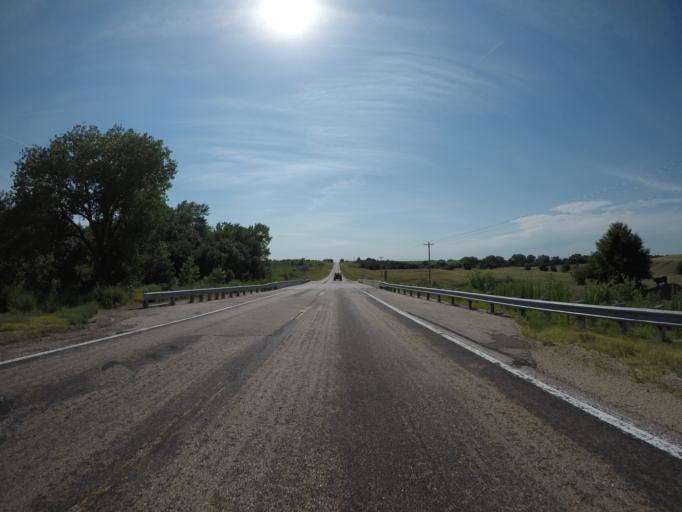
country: US
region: Nebraska
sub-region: Adams County
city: Hastings
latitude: 40.4663
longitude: -98.6233
